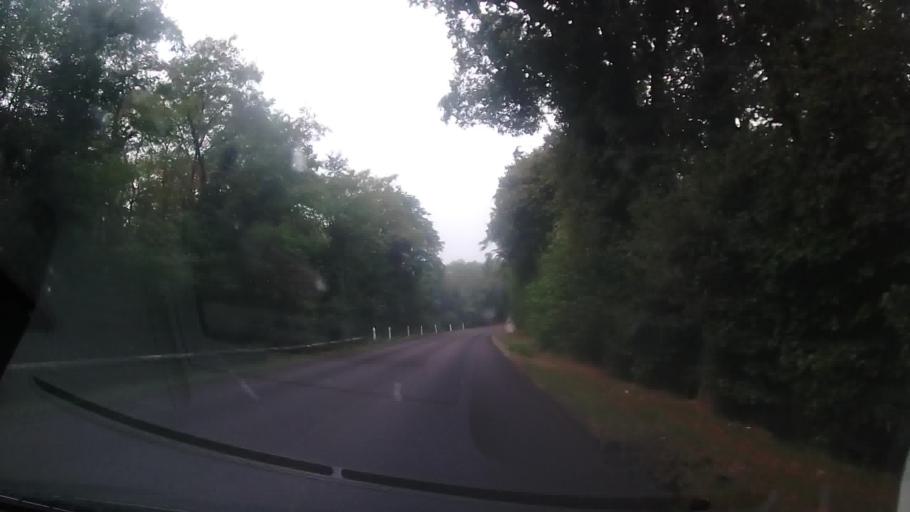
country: FR
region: Ile-de-France
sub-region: Departement de l'Essonne
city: Dourdan
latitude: 48.5386
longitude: 2.0008
